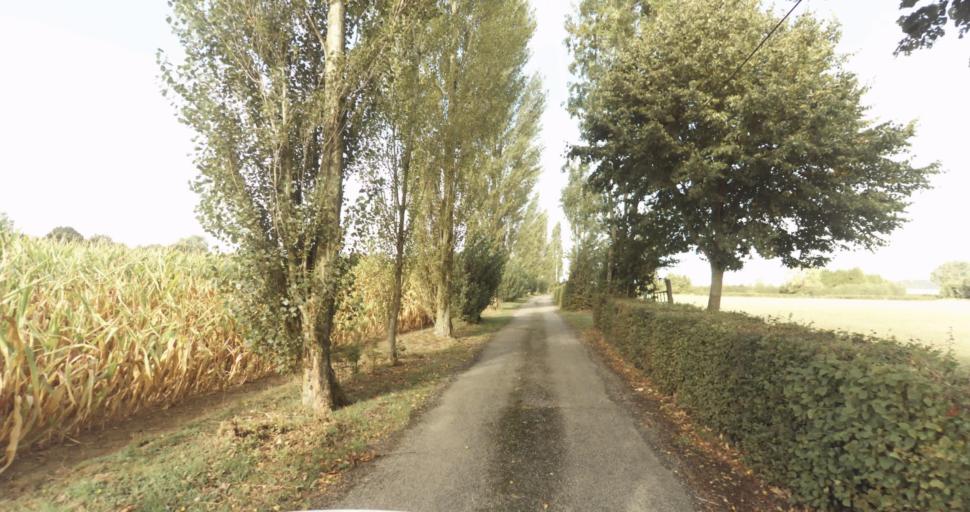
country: FR
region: Lower Normandy
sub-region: Departement de l'Orne
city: Gace
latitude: 48.8815
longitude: 0.3364
